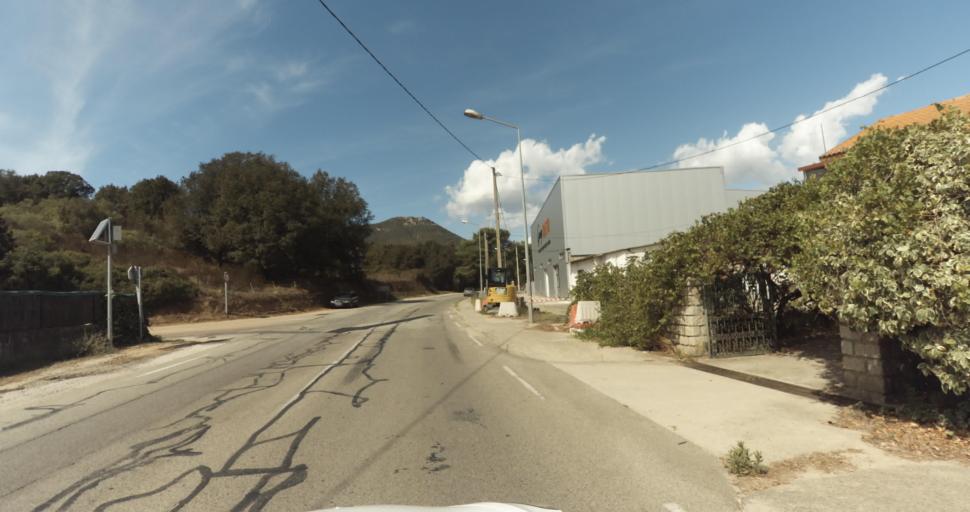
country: FR
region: Corsica
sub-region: Departement de la Corse-du-Sud
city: Afa
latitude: 41.9584
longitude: 8.7808
